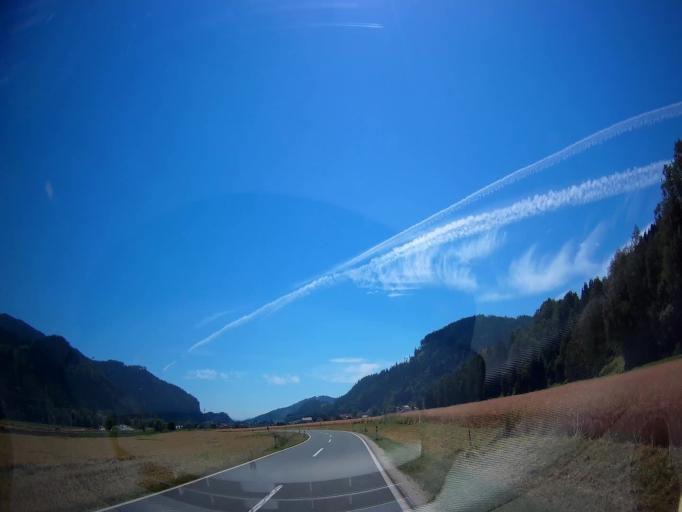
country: AT
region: Carinthia
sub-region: Politischer Bezirk Sankt Veit an der Glan
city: Micheldorf
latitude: 46.9231
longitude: 14.4278
